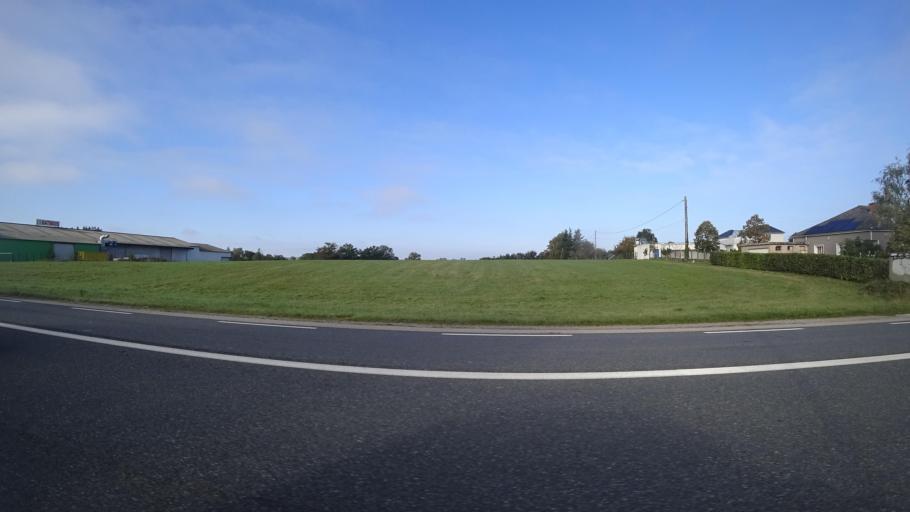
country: FR
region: Midi-Pyrenees
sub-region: Departement de l'Aveyron
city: Luc-la-Primaube
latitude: 44.3086
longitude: 2.5574
